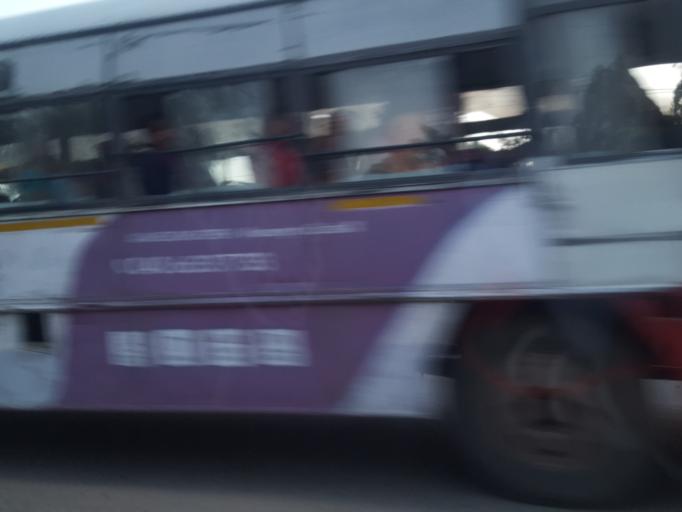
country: IN
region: Telangana
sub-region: Medak
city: Serilingampalle
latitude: 17.5264
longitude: 78.3545
